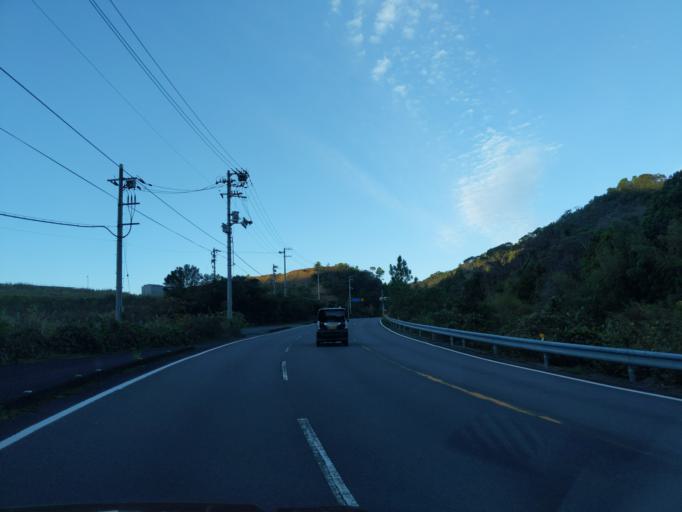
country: JP
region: Kochi
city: Muroto-misakicho
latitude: 33.6208
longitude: 134.3535
